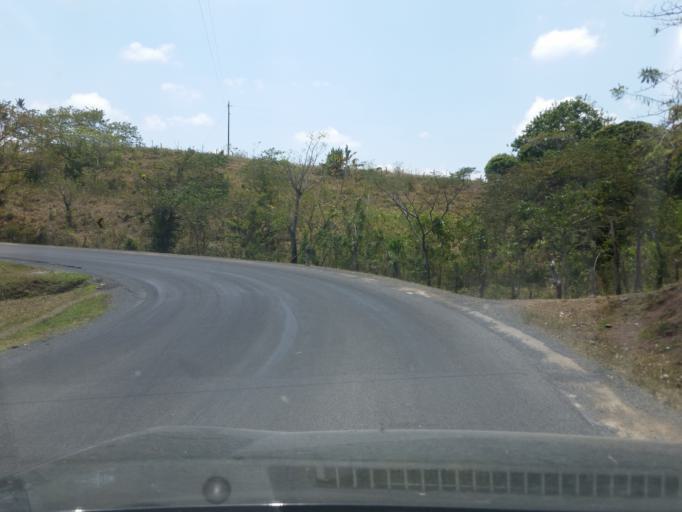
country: NI
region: Boaco
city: Boaco
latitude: 12.6066
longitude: -85.5391
